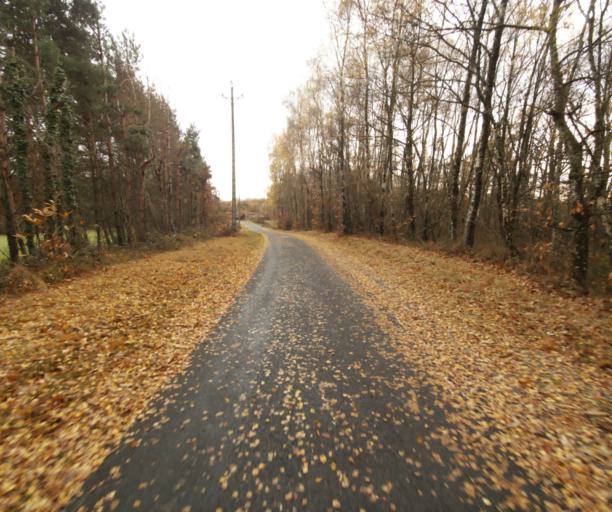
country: FR
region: Limousin
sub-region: Departement de la Correze
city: Sainte-Fortunade
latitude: 45.1896
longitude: 1.7546
